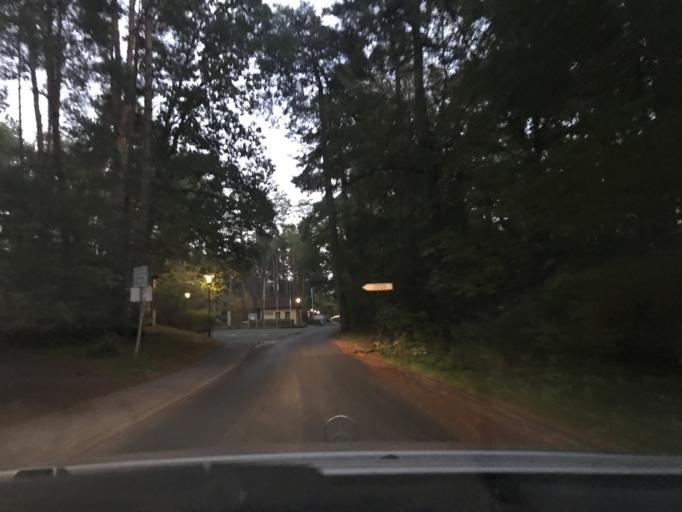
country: DE
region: Mecklenburg-Vorpommern
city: Karlshagen
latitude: 54.1189
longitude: 13.8433
